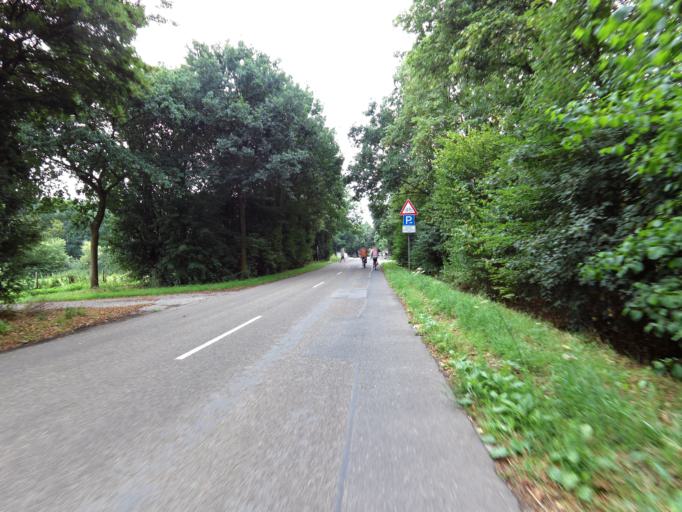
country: DE
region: North Rhine-Westphalia
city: Geilenkirchen
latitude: 50.9917
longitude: 6.1654
